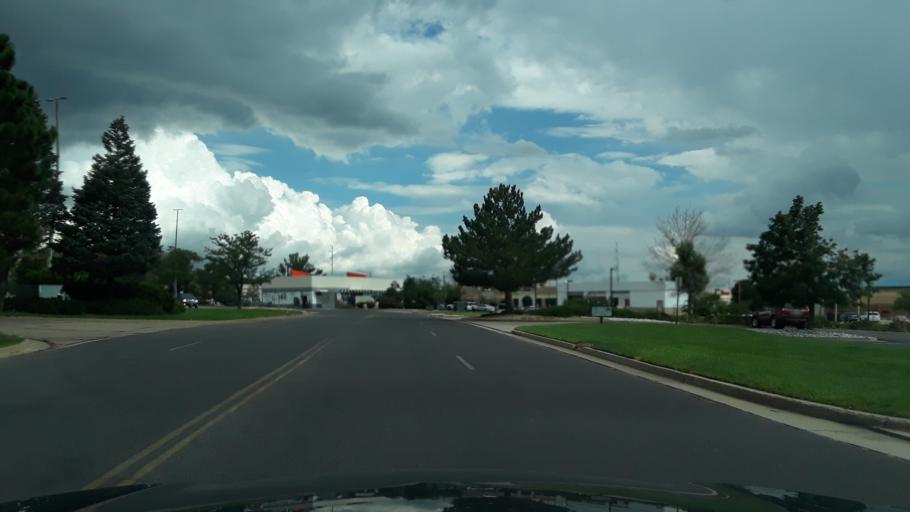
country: US
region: Colorado
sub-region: El Paso County
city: Air Force Academy
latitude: 38.9469
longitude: -104.8001
